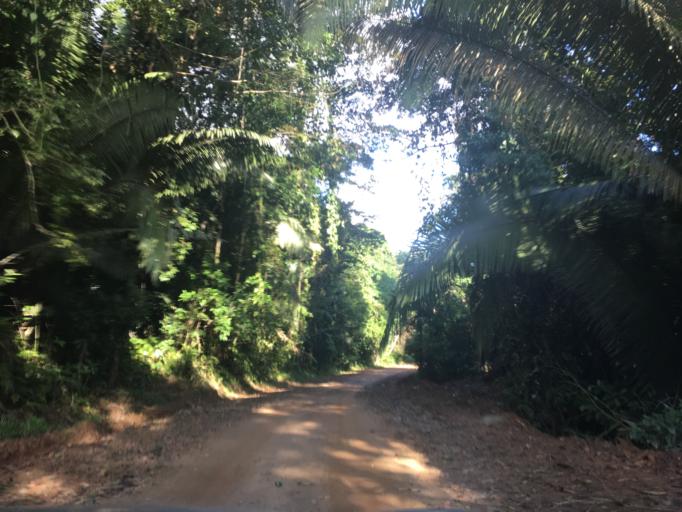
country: BZ
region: Stann Creek
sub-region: Dangriga
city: Dangriga
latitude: 16.7923
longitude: -88.4365
